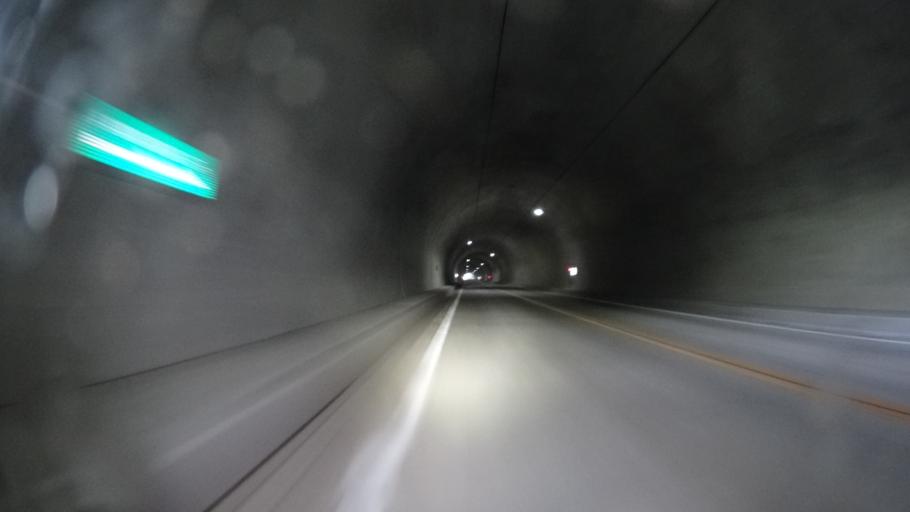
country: JP
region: Yamanashi
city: Enzan
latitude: 35.8049
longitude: 138.8645
